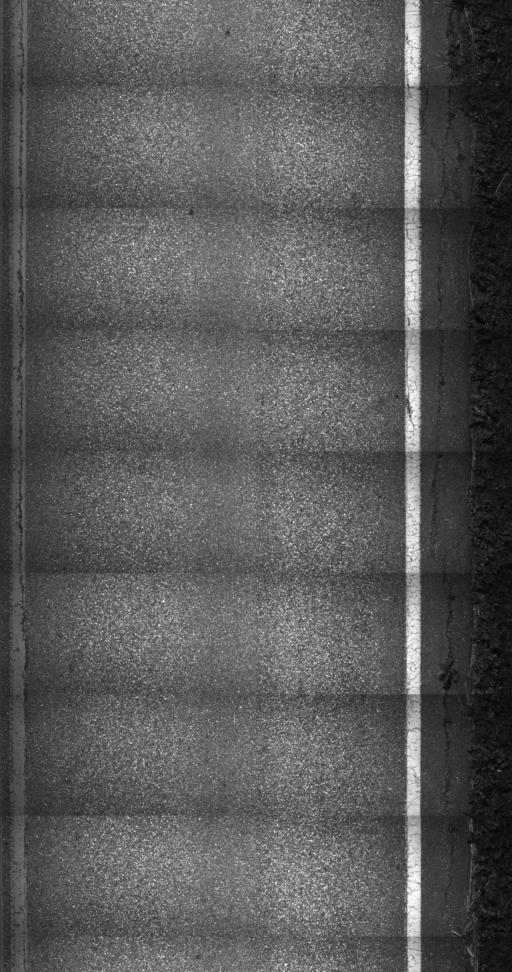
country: US
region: Vermont
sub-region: Rutland County
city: West Rutland
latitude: 43.5572
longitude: -73.0362
